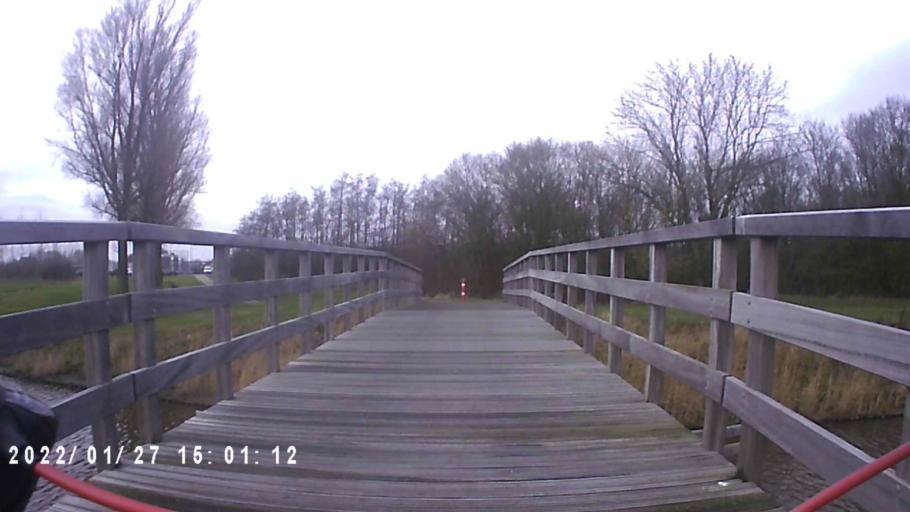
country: NL
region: Friesland
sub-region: Gemeente Dongeradeel
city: Anjum
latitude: 53.3706
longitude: 6.1548
